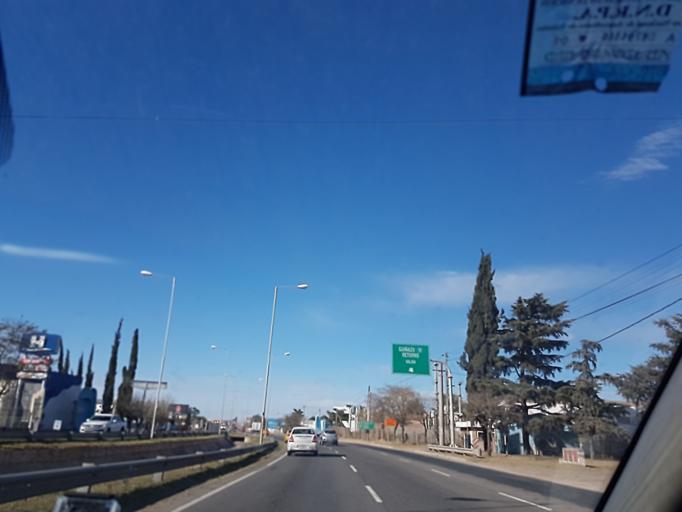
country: AR
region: Cordoba
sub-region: Departamento de Capital
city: Cordoba
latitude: -31.3314
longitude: -64.2103
